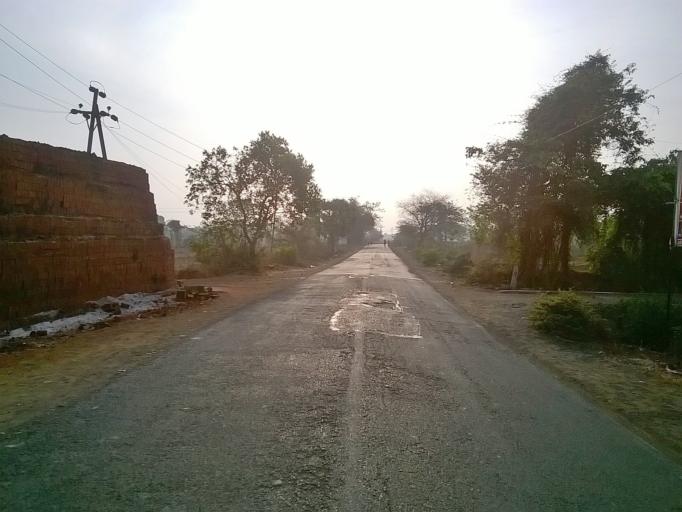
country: IN
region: Maharashtra
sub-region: Raigarh
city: Kalundri
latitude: 19.0126
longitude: 73.1602
